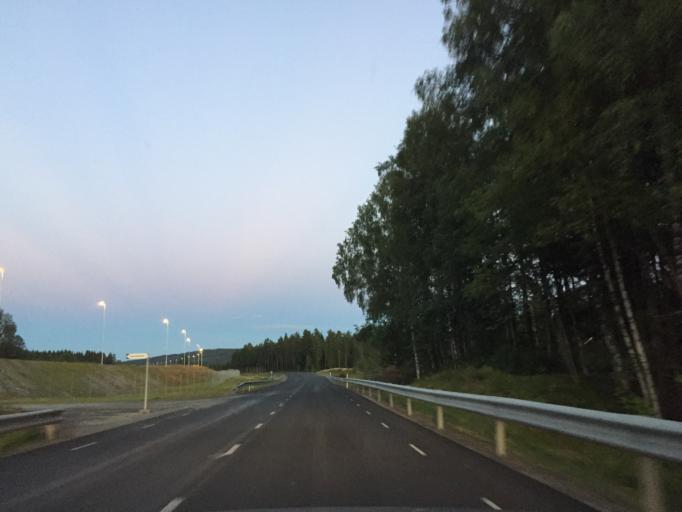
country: NO
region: Hedmark
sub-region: Kongsvinger
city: Spetalen
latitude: 60.2171
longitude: 11.8670
